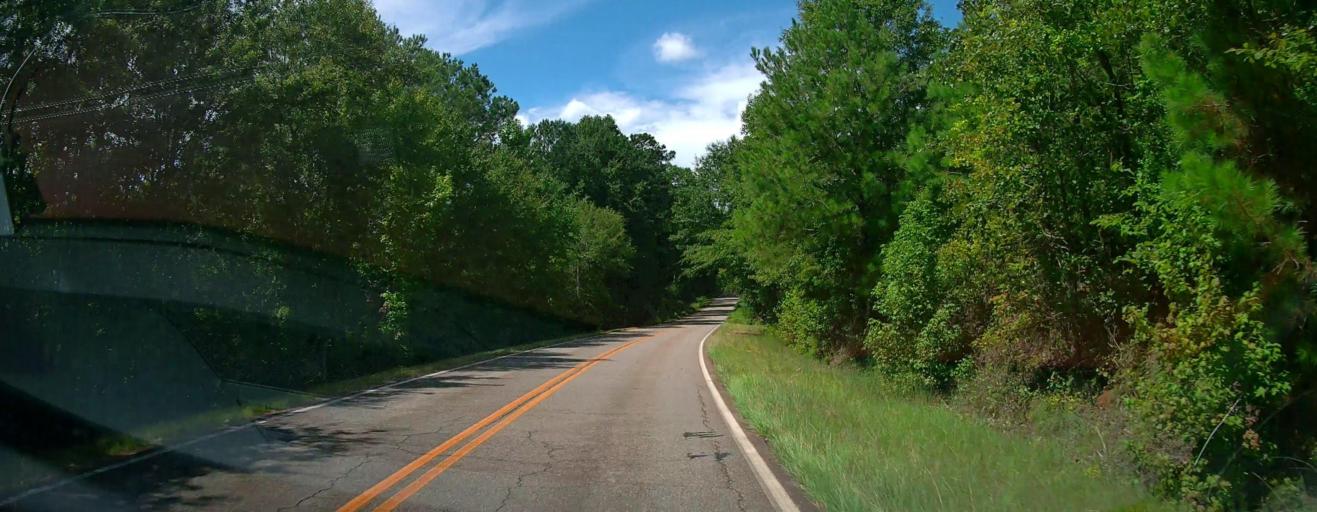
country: US
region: Georgia
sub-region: Peach County
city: Fort Valley
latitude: 32.5333
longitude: -83.8093
